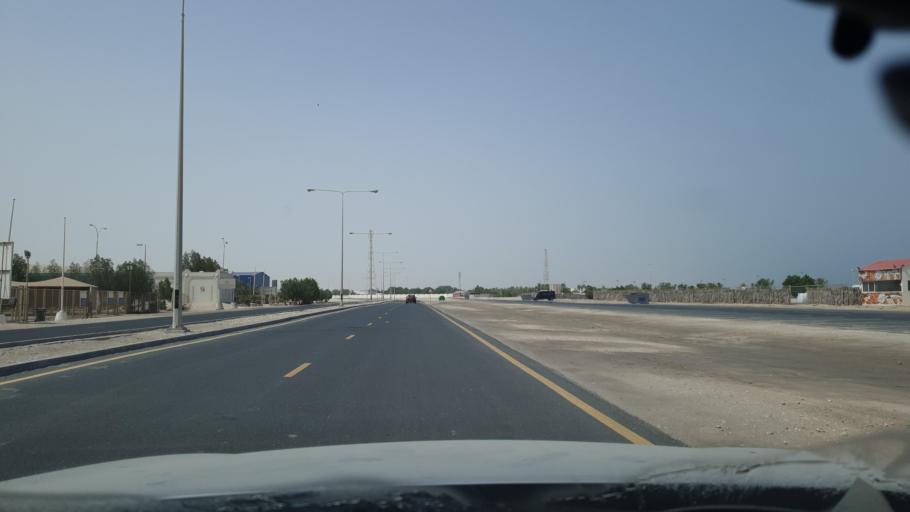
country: QA
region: Al Wakrah
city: Umm Sa'id
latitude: 24.8534
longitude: 51.5095
